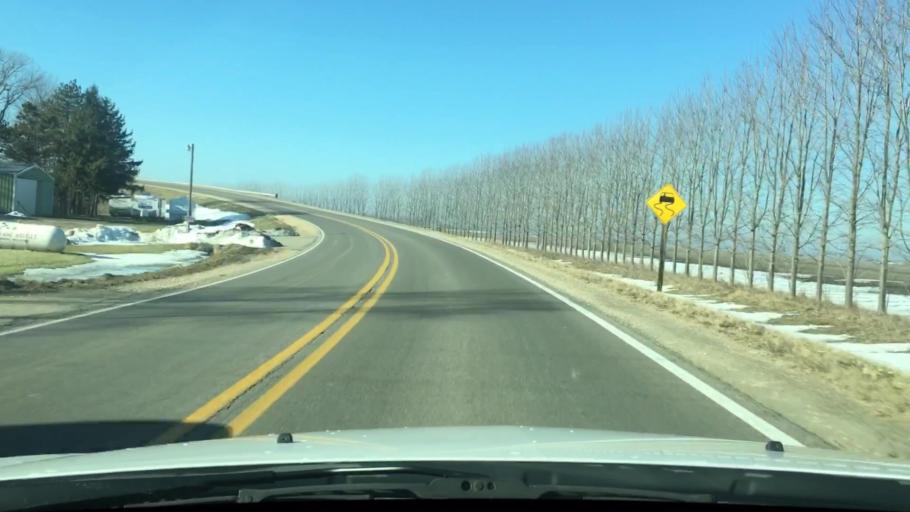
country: US
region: Illinois
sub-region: DeKalb County
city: Waterman
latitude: 41.7695
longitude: -88.8517
